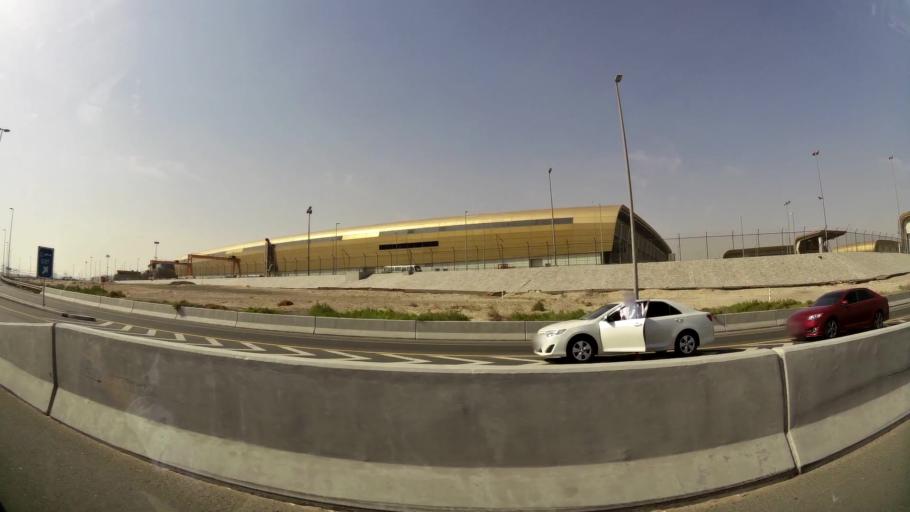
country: AE
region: Ash Shariqah
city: Sharjah
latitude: 25.2309
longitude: 55.4008
